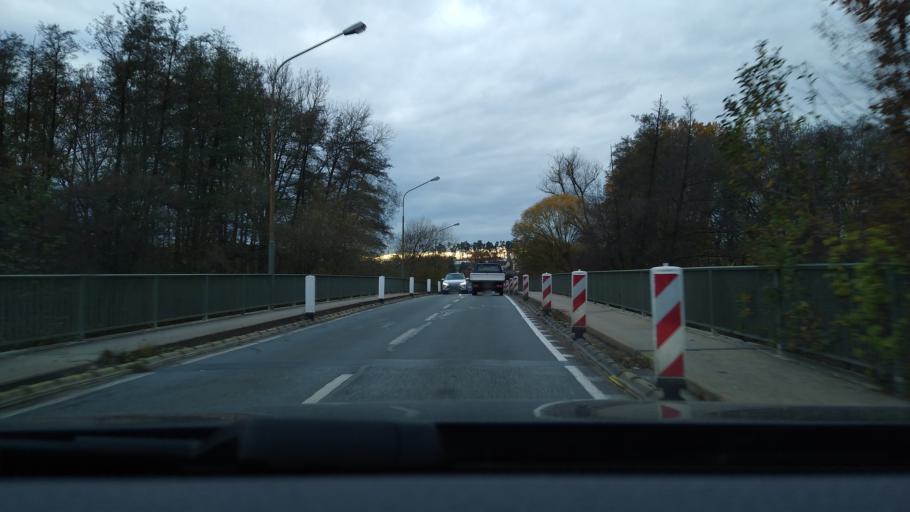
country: DE
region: Bavaria
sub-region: Regierungsbezirk Mittelfranken
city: Schwabach
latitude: 49.3491
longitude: 11.0551
